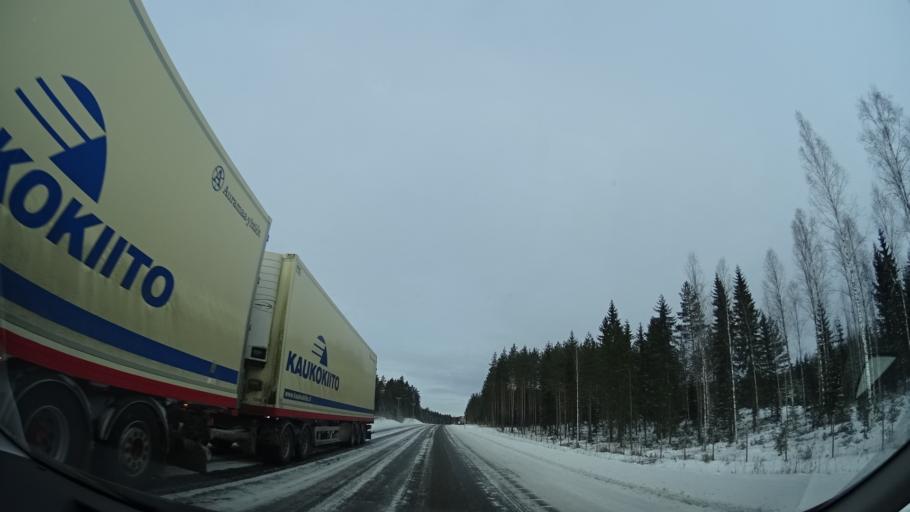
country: FI
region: Uusimaa
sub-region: Helsinki
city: Kaerkoelae
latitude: 60.6424
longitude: 23.8818
